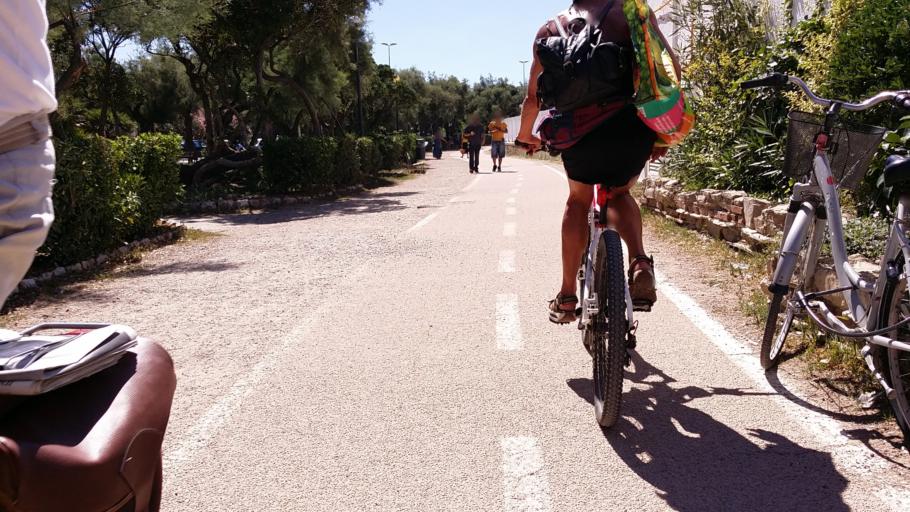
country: IT
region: Tuscany
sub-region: Provincia di Livorno
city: Livorno
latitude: 43.5159
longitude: 10.3164
